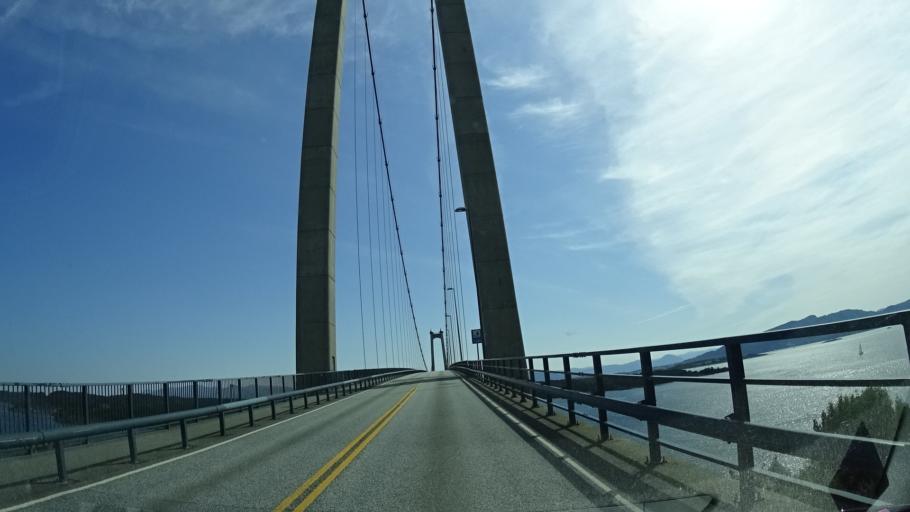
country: NO
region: Hordaland
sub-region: Bomlo
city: Mosterhamn
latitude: 59.7366
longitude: 5.3711
